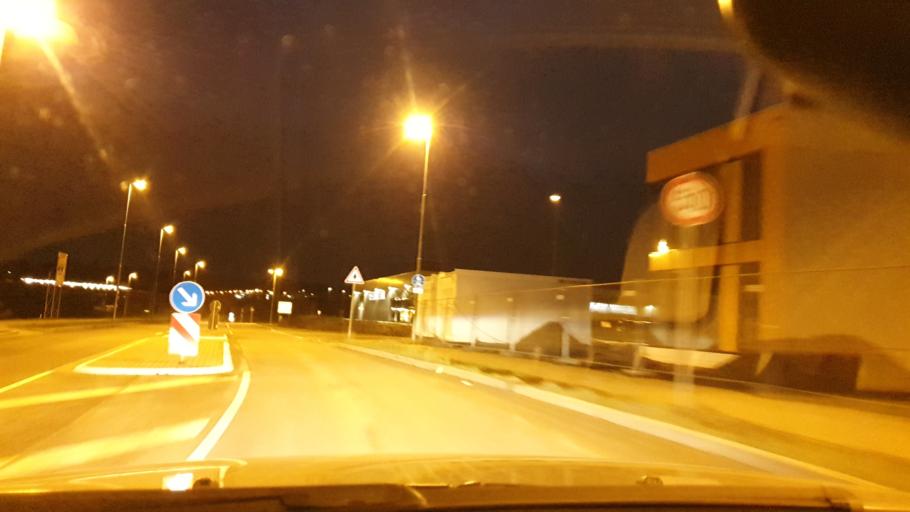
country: DE
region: Rheinland-Pfalz
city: Katzweiler
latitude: 49.4772
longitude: 7.6820
